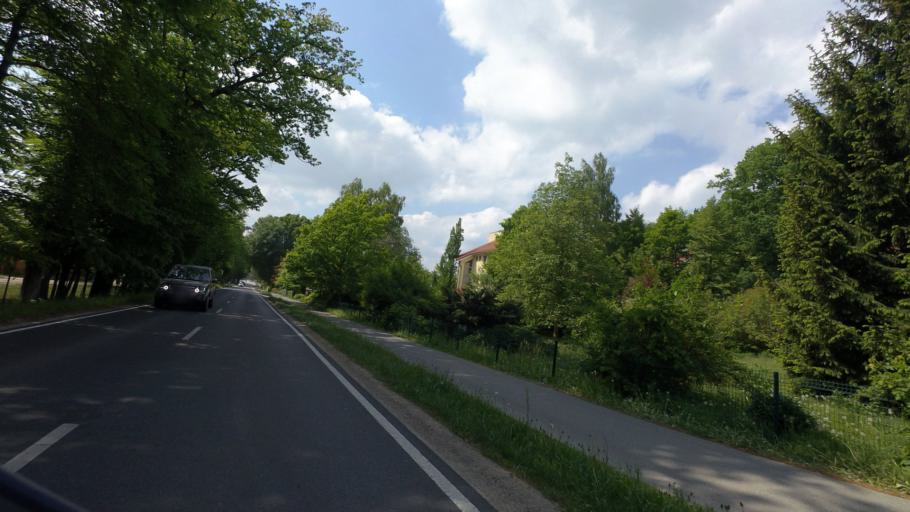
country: DE
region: Saxony
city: Niesky
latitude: 51.2939
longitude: 14.8155
